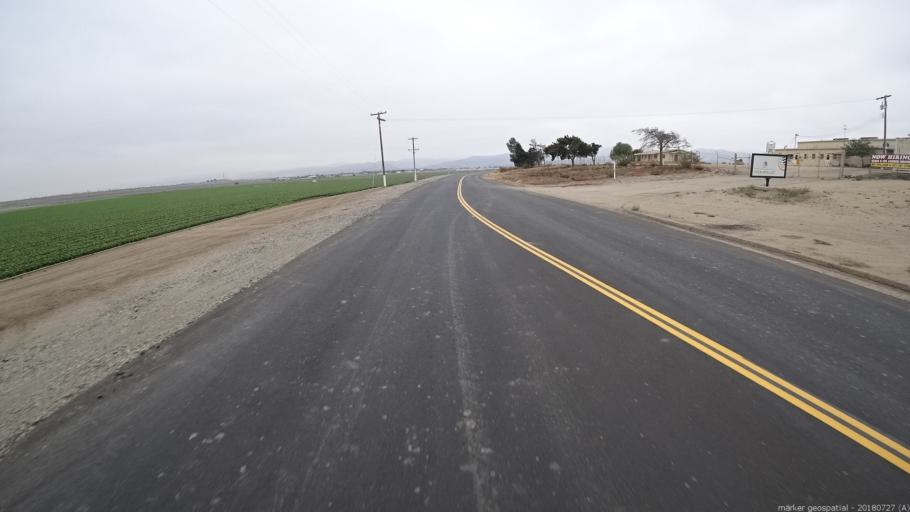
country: US
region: California
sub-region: Monterey County
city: King City
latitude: 36.2252
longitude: -121.1124
